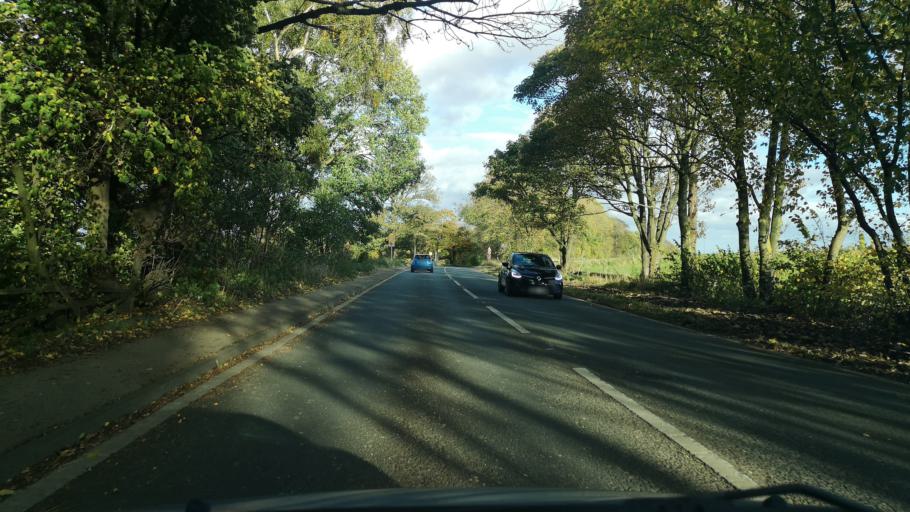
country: GB
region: England
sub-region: City and Borough of Wakefield
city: Middlestown
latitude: 53.6387
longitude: -1.6337
